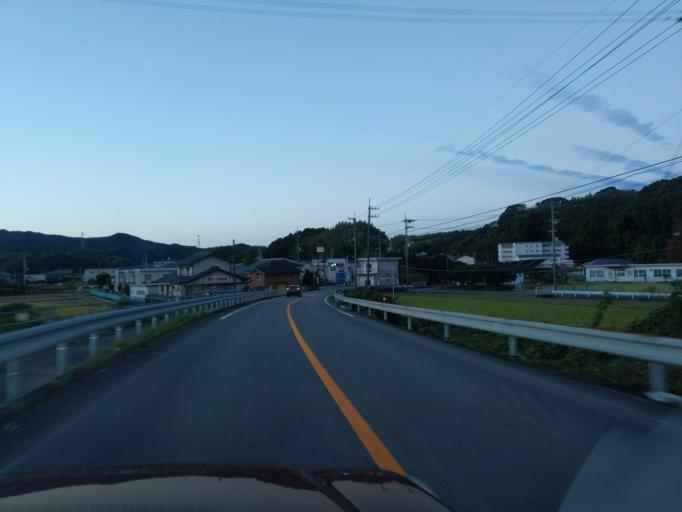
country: JP
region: Tokushima
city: Anan
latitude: 33.8434
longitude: 134.6244
